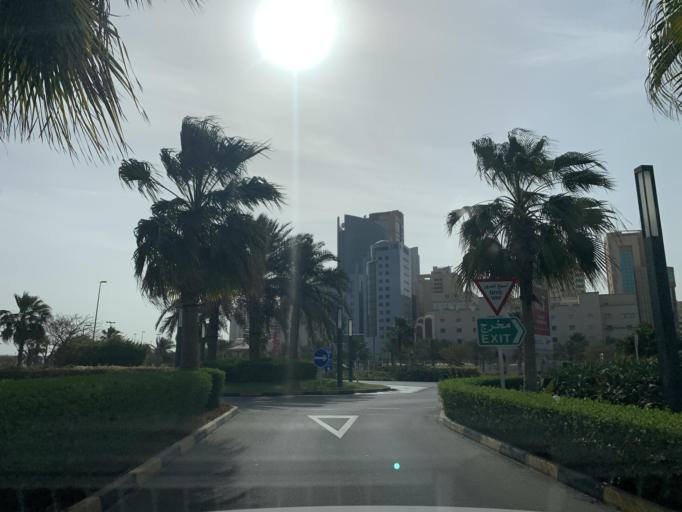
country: BH
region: Muharraq
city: Al Muharraq
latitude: 26.2450
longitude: 50.5863
